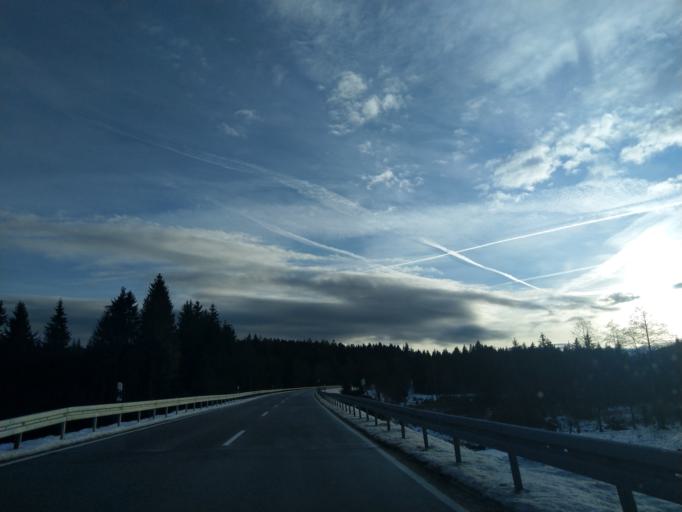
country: DE
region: Bavaria
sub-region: Lower Bavaria
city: Bischofsmais
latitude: 48.8851
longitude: 13.0924
